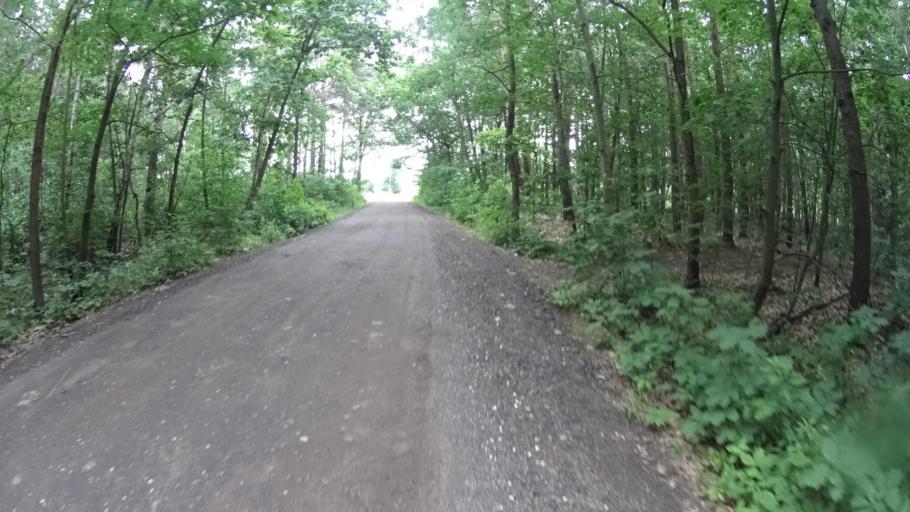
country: PL
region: Masovian Voivodeship
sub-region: Powiat pruszkowski
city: Nadarzyn
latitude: 52.0636
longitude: 20.8214
